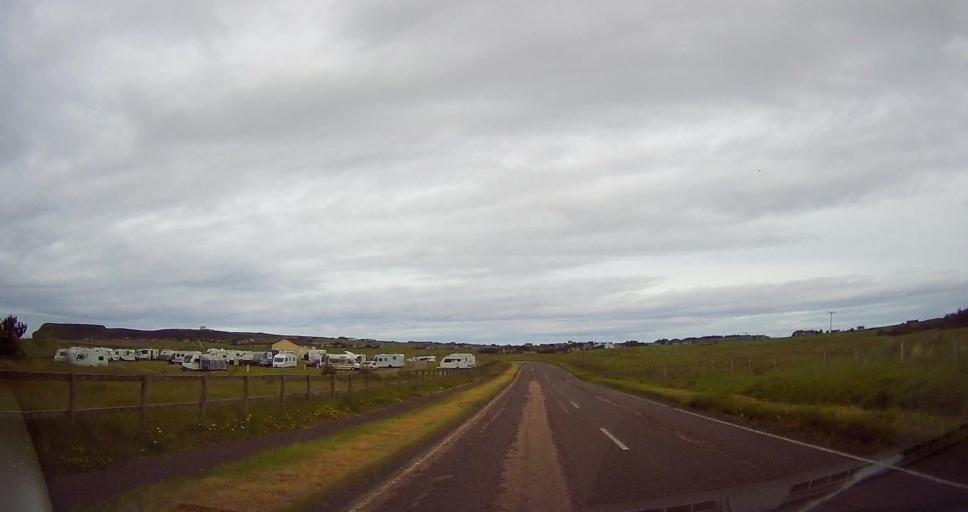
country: GB
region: Scotland
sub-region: Highland
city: Thurso
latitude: 58.6133
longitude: -3.3434
